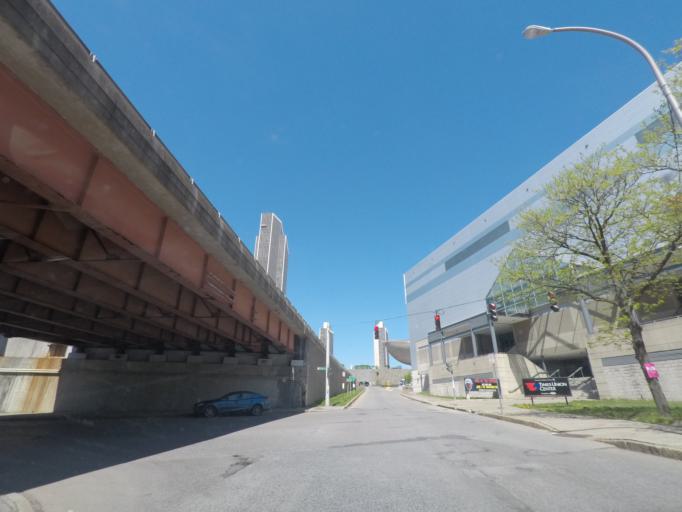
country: US
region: New York
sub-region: Albany County
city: Albany
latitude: 42.6479
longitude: -73.7549
